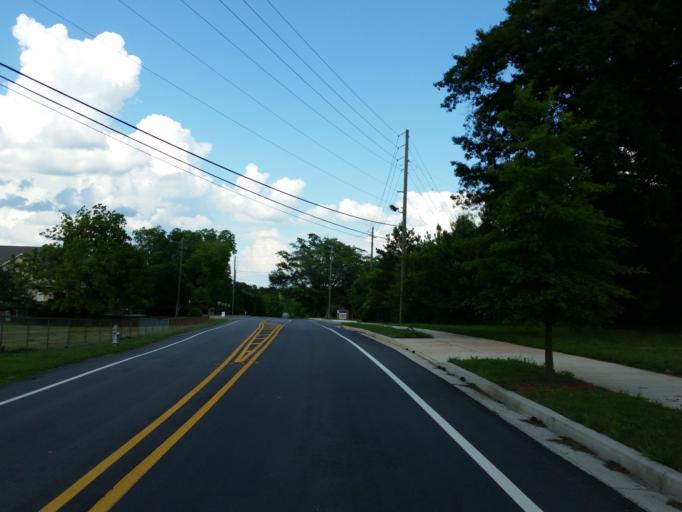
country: US
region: Georgia
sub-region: Fulton County
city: Roswell
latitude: 34.0607
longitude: -84.3396
